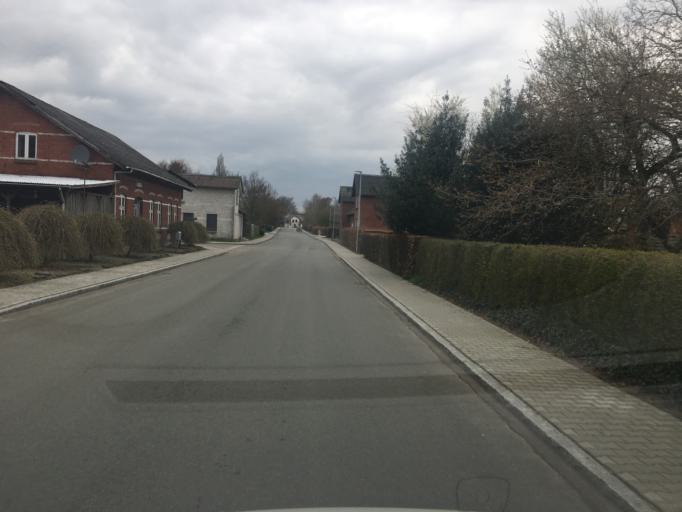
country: DK
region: South Denmark
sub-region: Tonder Kommune
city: Toftlund
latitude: 55.0599
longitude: 9.1062
